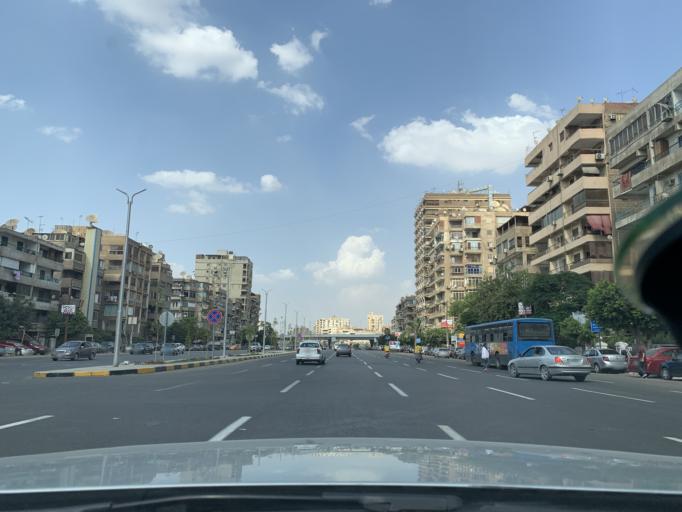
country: EG
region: Muhafazat al Qalyubiyah
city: Al Khankah
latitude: 30.1098
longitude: 31.3425
